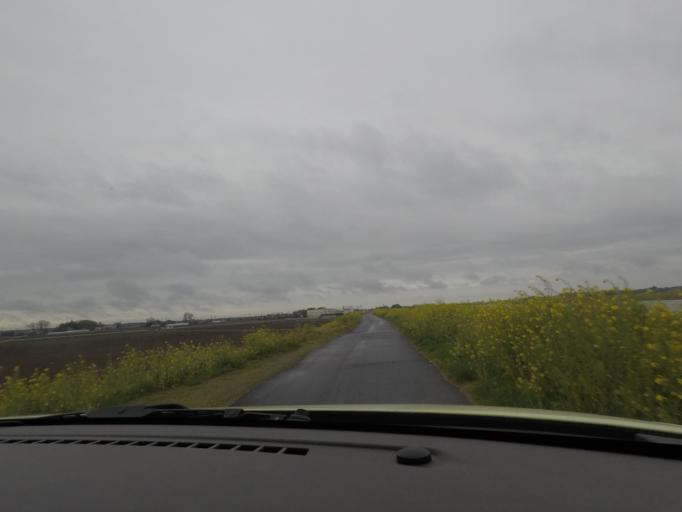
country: JP
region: Ibaraki
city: Mitsukaido
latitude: 36.0519
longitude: 140.0226
